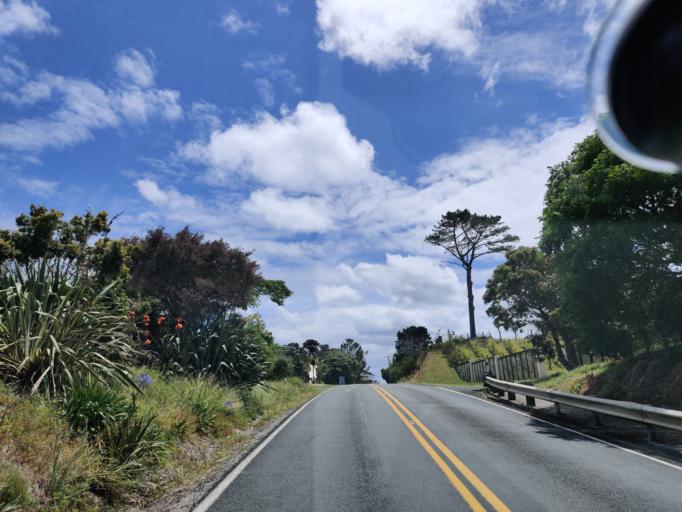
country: NZ
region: Northland
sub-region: Far North District
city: Kaitaia
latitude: -34.8103
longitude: 173.1160
